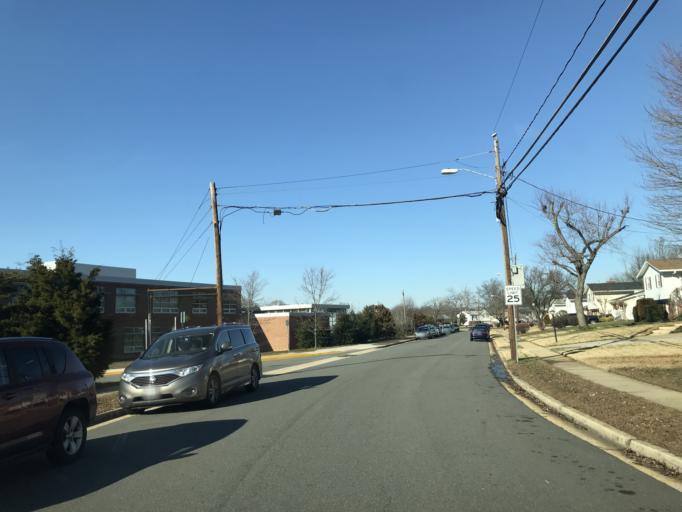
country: US
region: Virginia
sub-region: Fairfax County
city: Franconia
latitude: 38.7843
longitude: -77.1636
